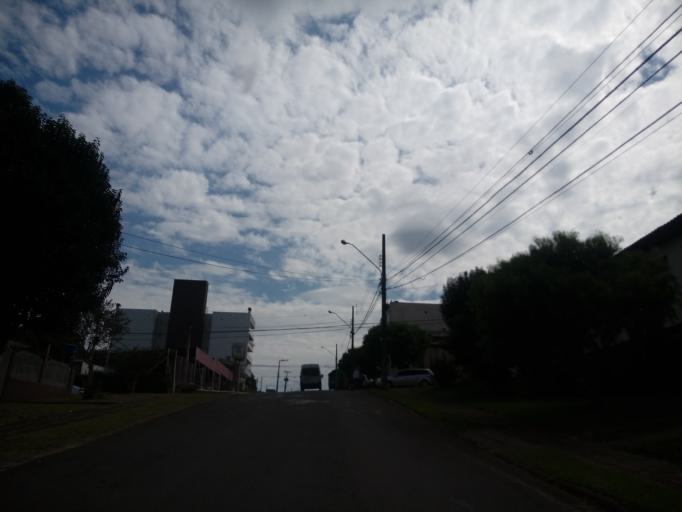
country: BR
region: Santa Catarina
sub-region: Chapeco
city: Chapeco
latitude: -27.1067
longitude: -52.6041
